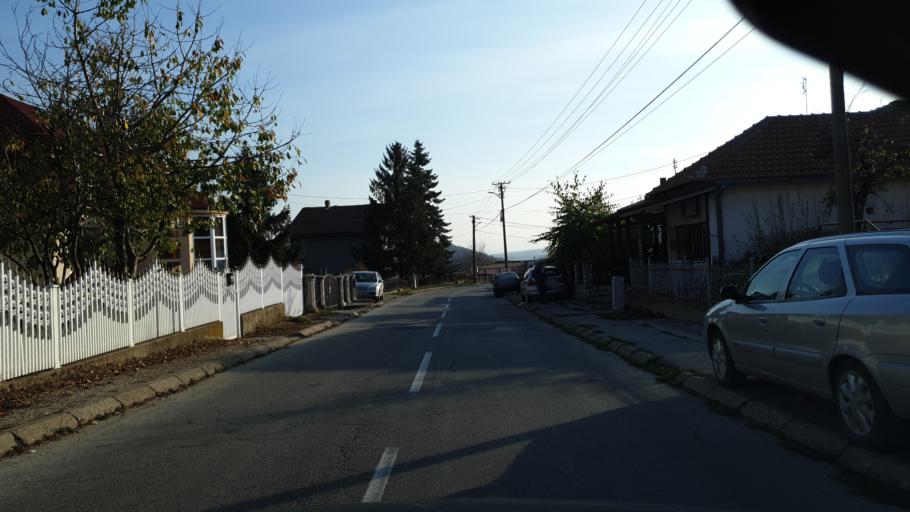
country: RS
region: Central Serbia
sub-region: Borski Okrug
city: Bor
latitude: 44.0525
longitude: 22.1011
